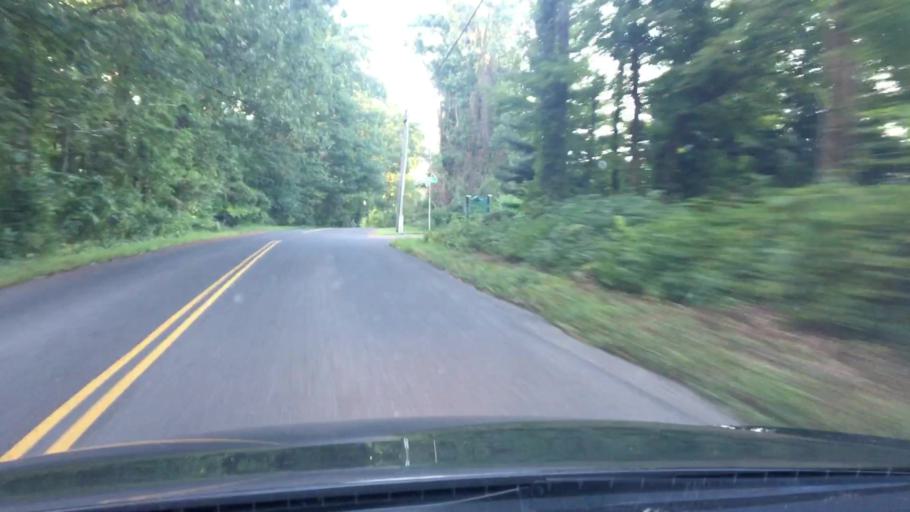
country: US
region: Connecticut
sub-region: Litchfield County
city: New Milford
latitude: 41.6145
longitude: -73.3727
